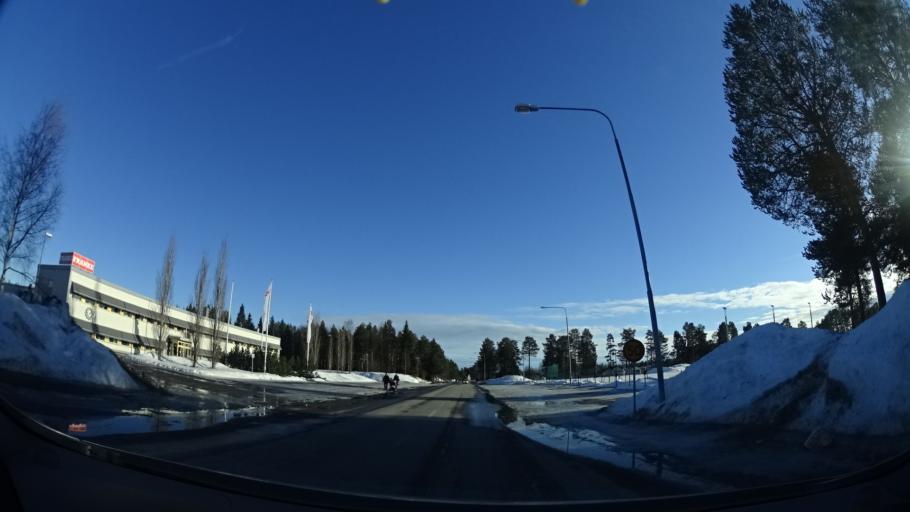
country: SE
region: Vaesterbotten
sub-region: Skelleftea Kommun
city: Byske
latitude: 64.9558
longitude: 21.2104
